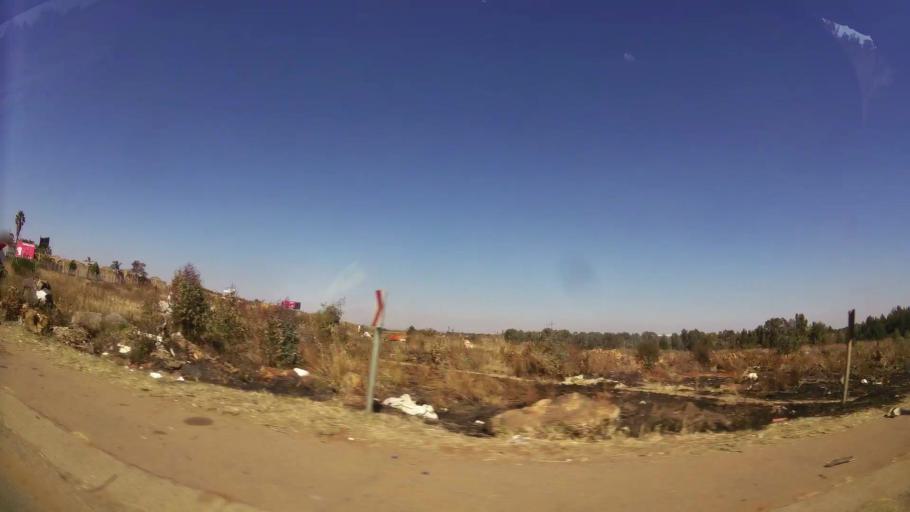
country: ZA
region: Gauteng
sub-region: City of Tshwane Metropolitan Municipality
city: Centurion
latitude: -25.8504
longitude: 28.2248
